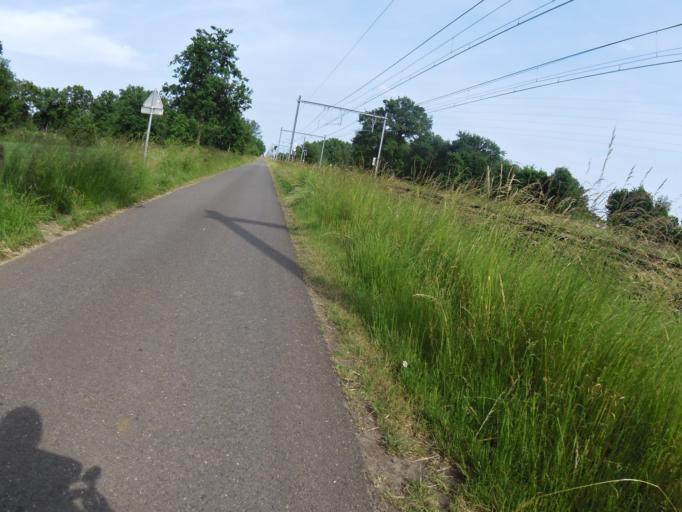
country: BE
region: Flanders
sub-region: Provincie Antwerpen
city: Olen
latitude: 51.1734
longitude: 4.9098
